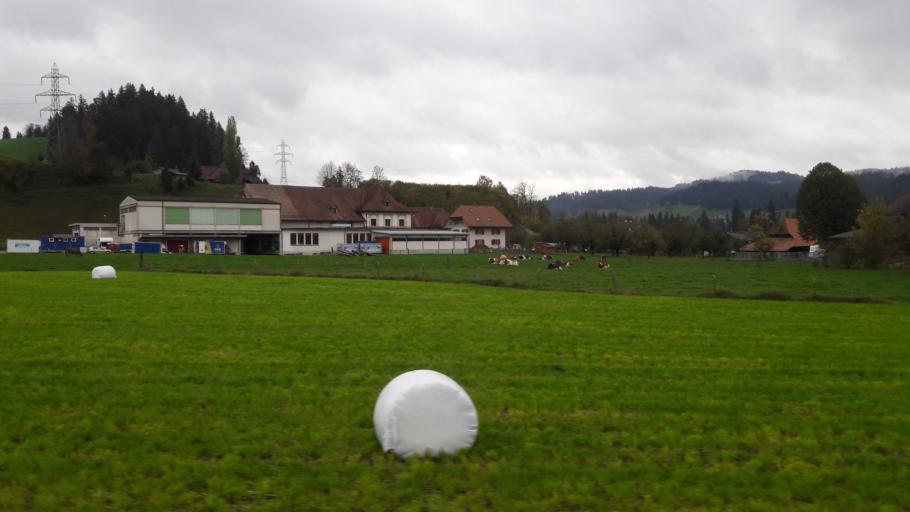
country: CH
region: Bern
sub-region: Emmental District
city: Lutzelfluh
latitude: 47.0012
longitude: 7.7091
